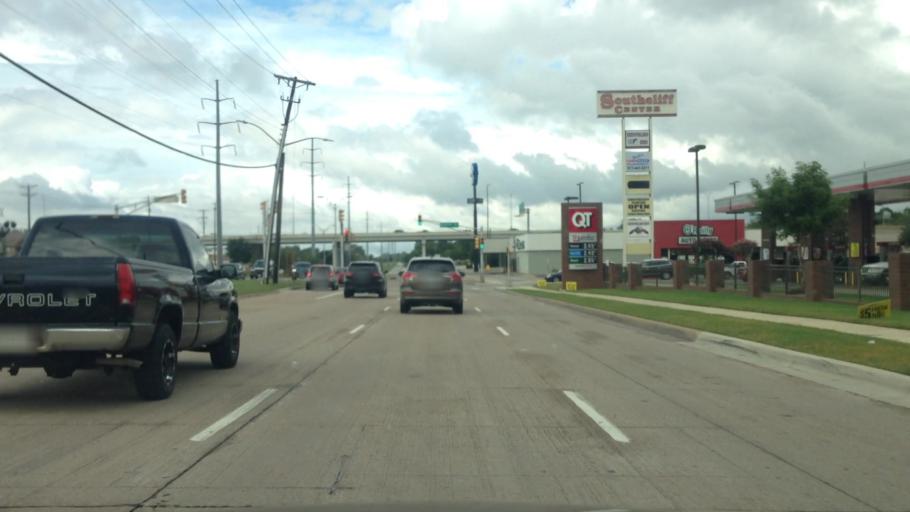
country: US
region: Texas
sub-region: Tarrant County
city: Edgecliff Village
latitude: 32.6728
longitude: -97.3833
